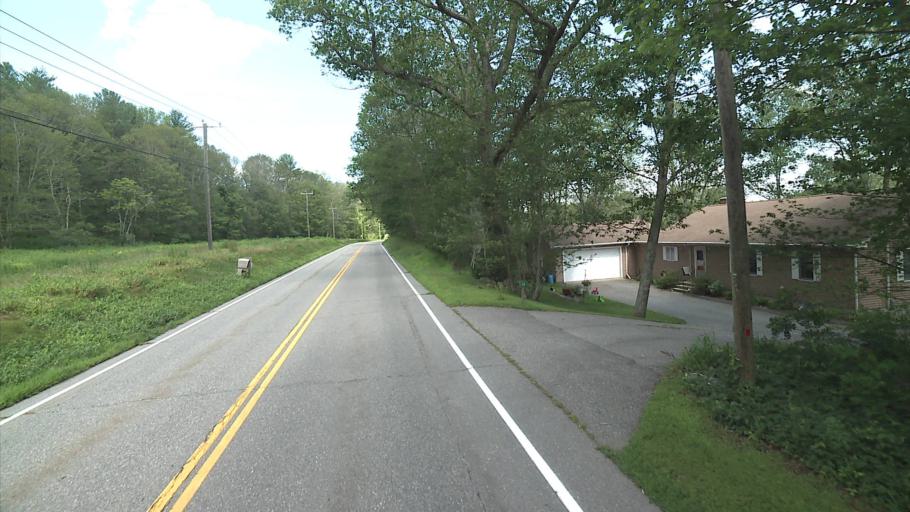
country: US
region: Connecticut
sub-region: Windham County
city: South Woodstock
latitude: 41.8623
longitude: -72.0926
